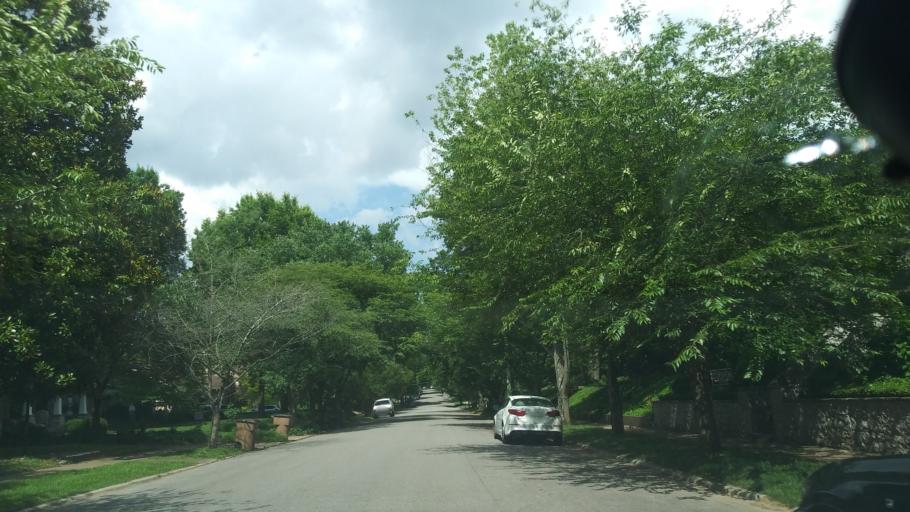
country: US
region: Tennessee
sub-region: Davidson County
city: Belle Meade
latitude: 36.1366
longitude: -86.8277
